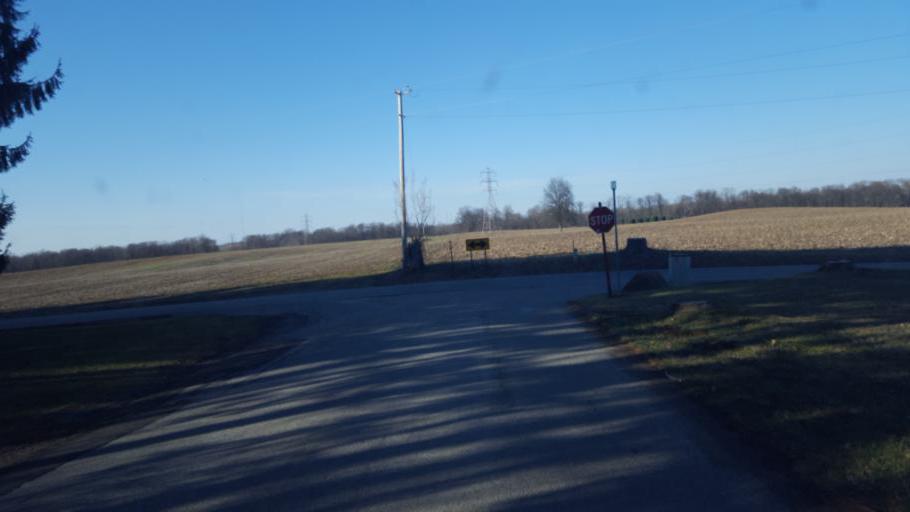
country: US
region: Ohio
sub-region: Richland County
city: Ontario
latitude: 40.7467
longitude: -82.6087
